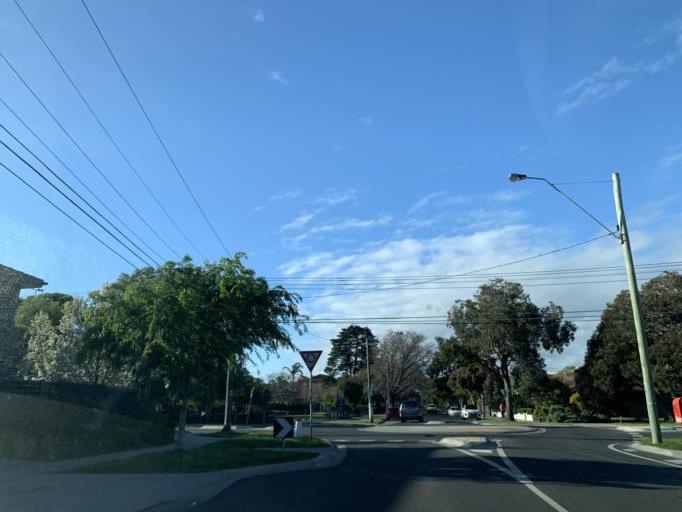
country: AU
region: Victoria
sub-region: Kingston
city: Mentone
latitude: -37.9863
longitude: 145.0647
